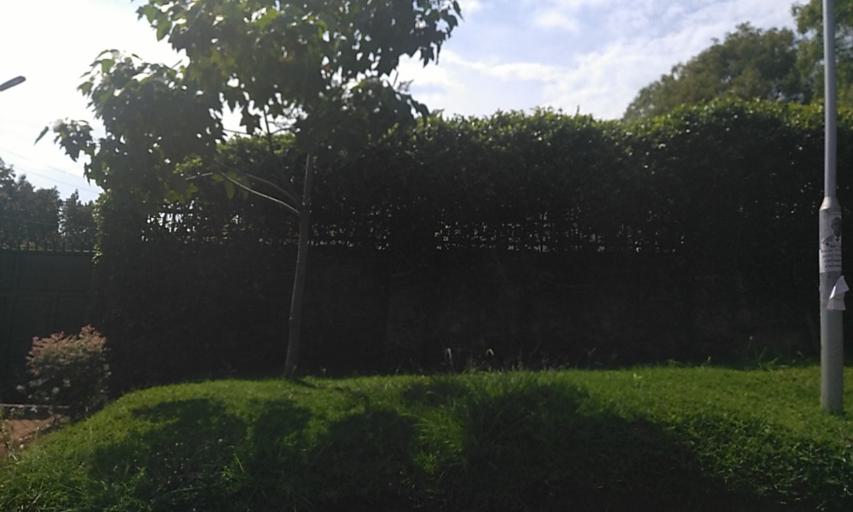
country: UG
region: Central Region
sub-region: Wakiso District
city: Kireka
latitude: 0.3564
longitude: 32.6174
